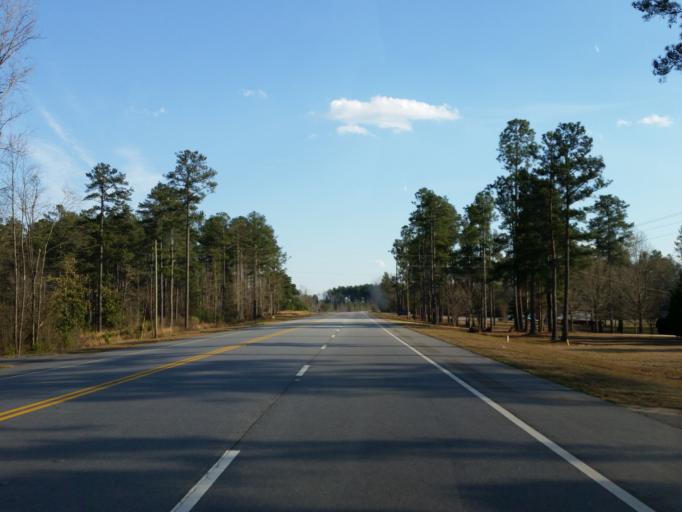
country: US
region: Georgia
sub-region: Monroe County
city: Forsyth
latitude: 33.0409
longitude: -84.0050
